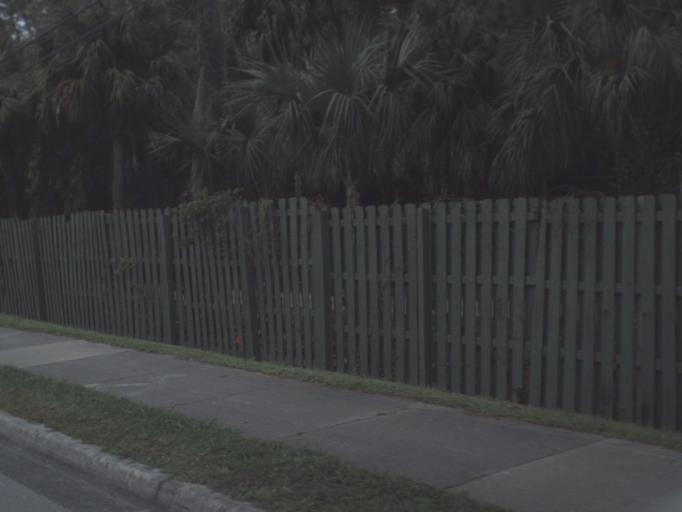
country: US
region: Florida
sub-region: Collier County
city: Lely
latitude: 26.1342
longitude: -81.6870
